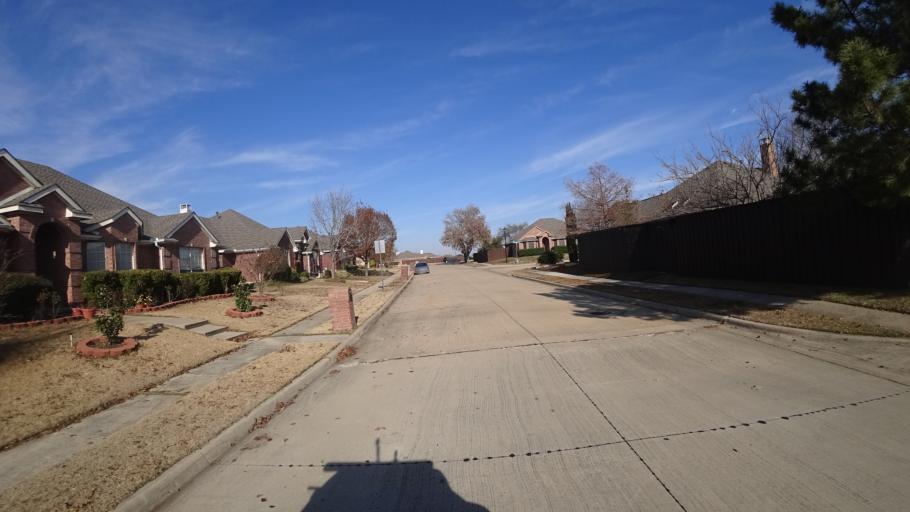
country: US
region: Texas
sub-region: Denton County
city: Lewisville
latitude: 33.0487
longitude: -97.0192
